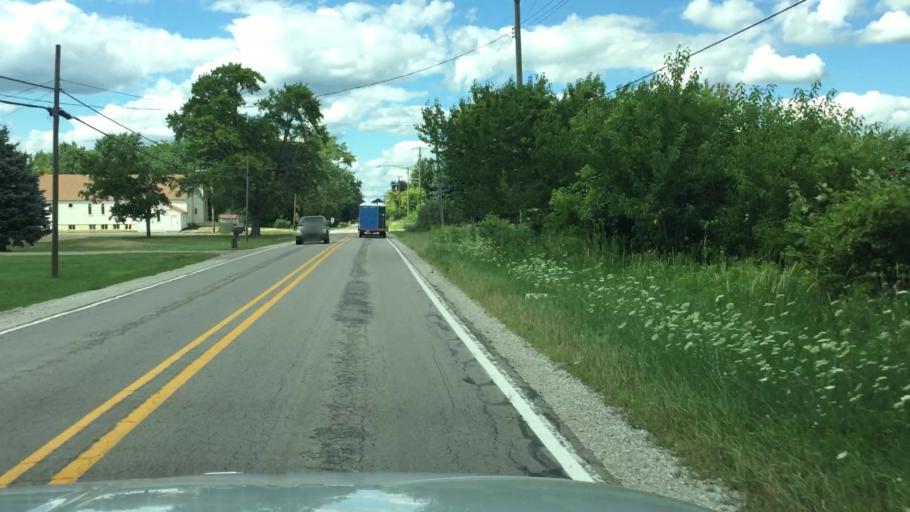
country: US
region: Michigan
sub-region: Saint Clair County
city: Capac
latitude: 42.9191
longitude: -82.9455
